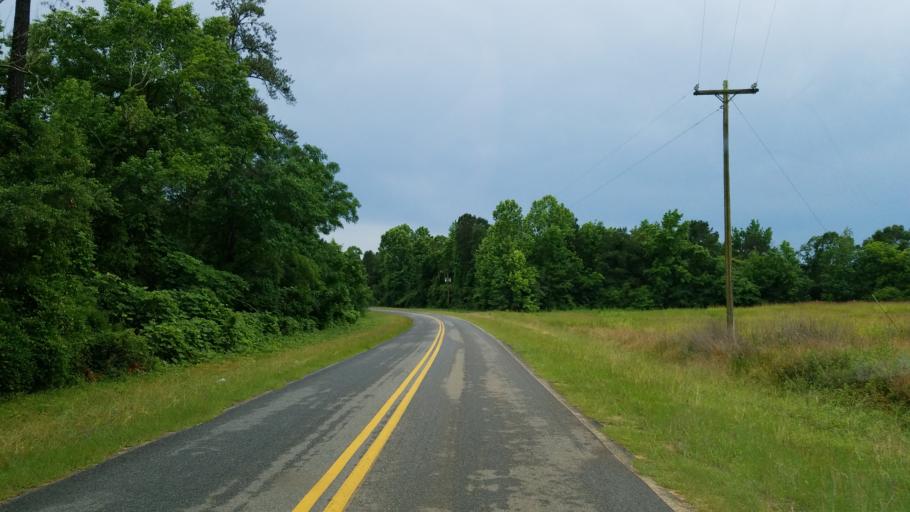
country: US
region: Georgia
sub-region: Dooly County
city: Unadilla
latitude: 32.2345
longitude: -83.7979
